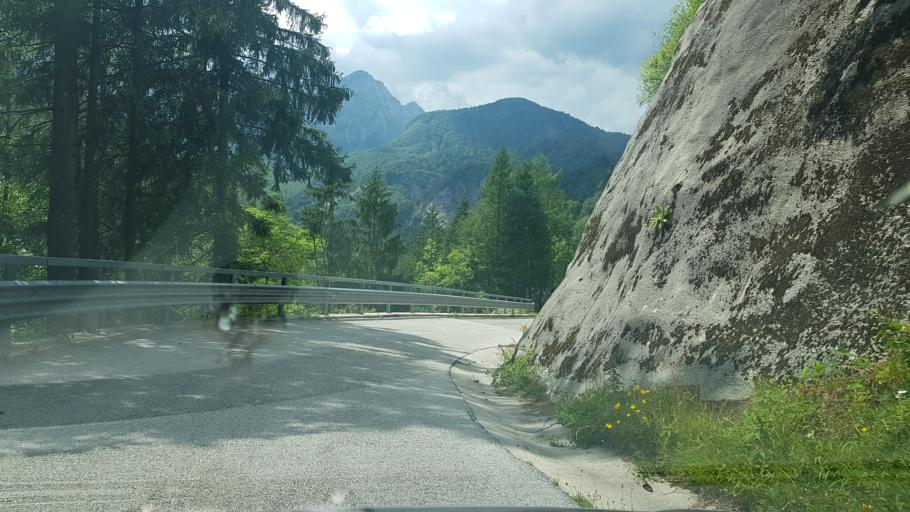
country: IT
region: Friuli Venezia Giulia
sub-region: Provincia di Udine
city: Moggio Udinese
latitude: 46.4950
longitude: 13.2181
